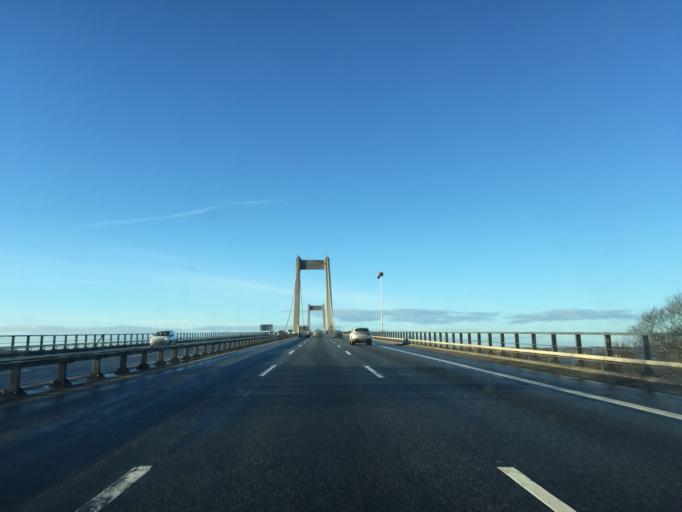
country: DK
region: South Denmark
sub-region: Middelfart Kommune
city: Strib
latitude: 55.5161
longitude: 9.7625
